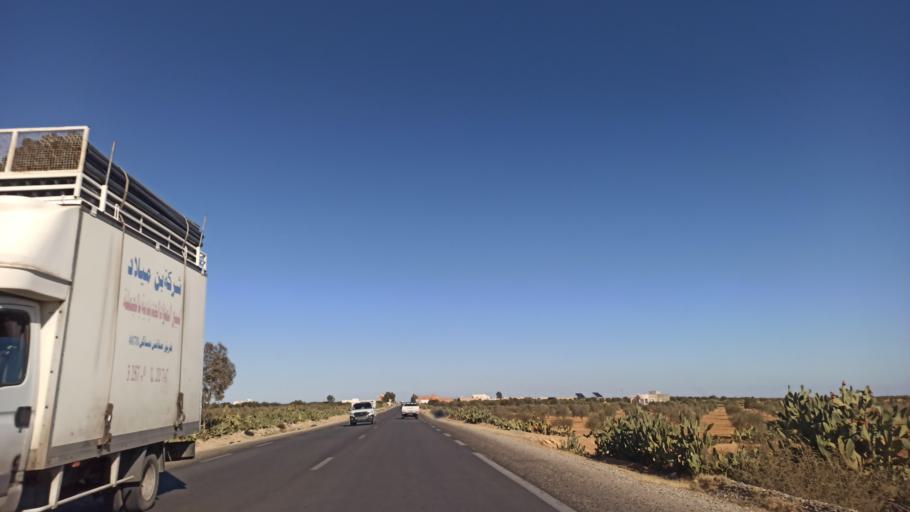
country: TN
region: Sidi Bu Zayd
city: Bi'r al Hufayy
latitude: 34.9659
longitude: 9.2254
